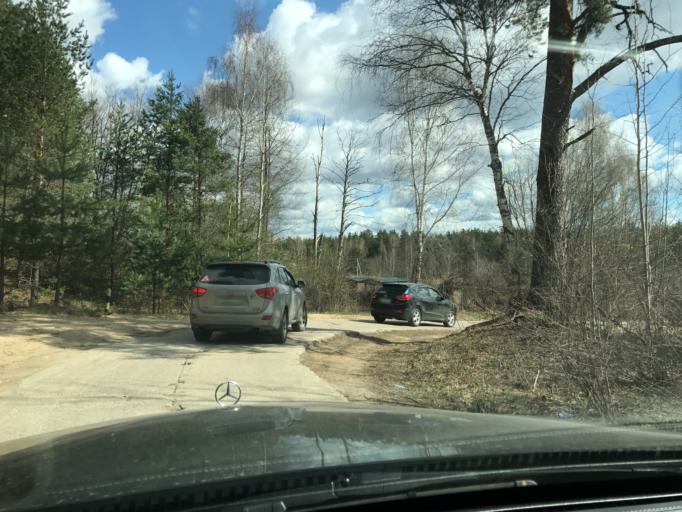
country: RU
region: Moskovskaya
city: Vereya
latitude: 55.8395
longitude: 39.0794
